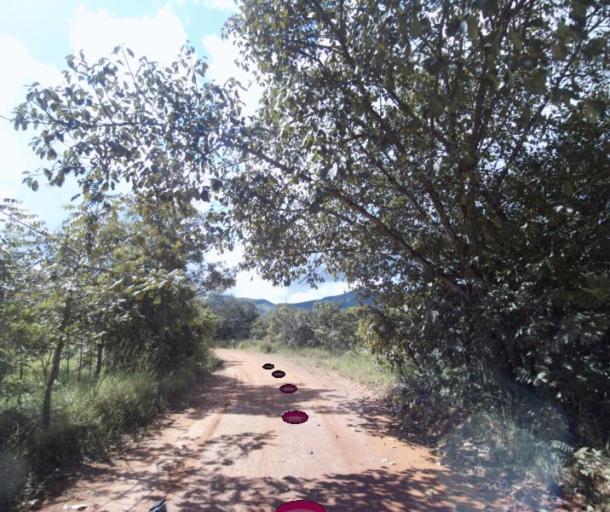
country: BR
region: Goias
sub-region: Pirenopolis
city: Pirenopolis
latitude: -15.7765
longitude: -48.9938
